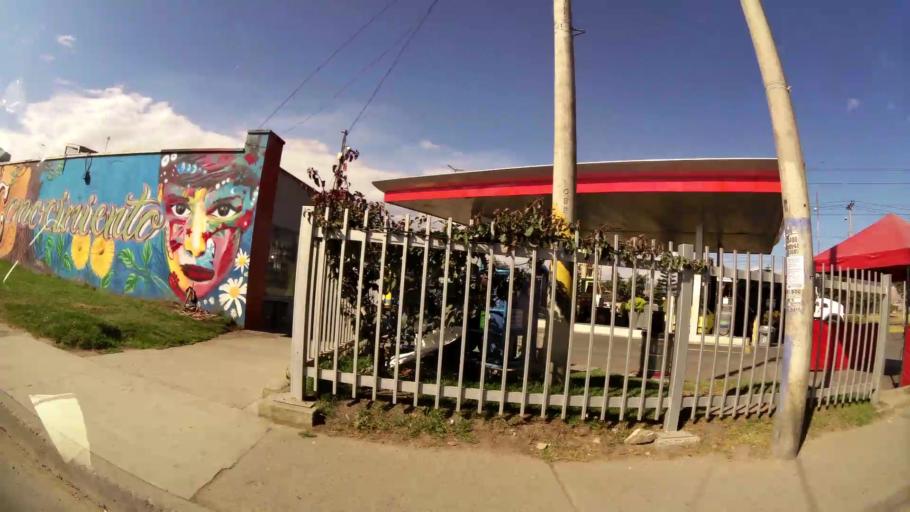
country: CO
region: Bogota D.C.
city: Bogota
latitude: 4.5465
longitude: -74.1374
